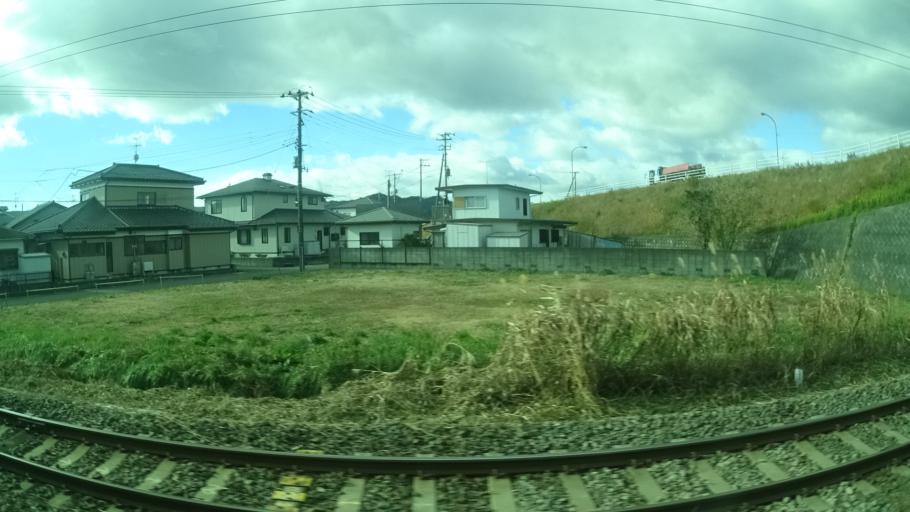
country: JP
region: Miyagi
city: Watari
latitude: 38.0369
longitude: 140.8635
